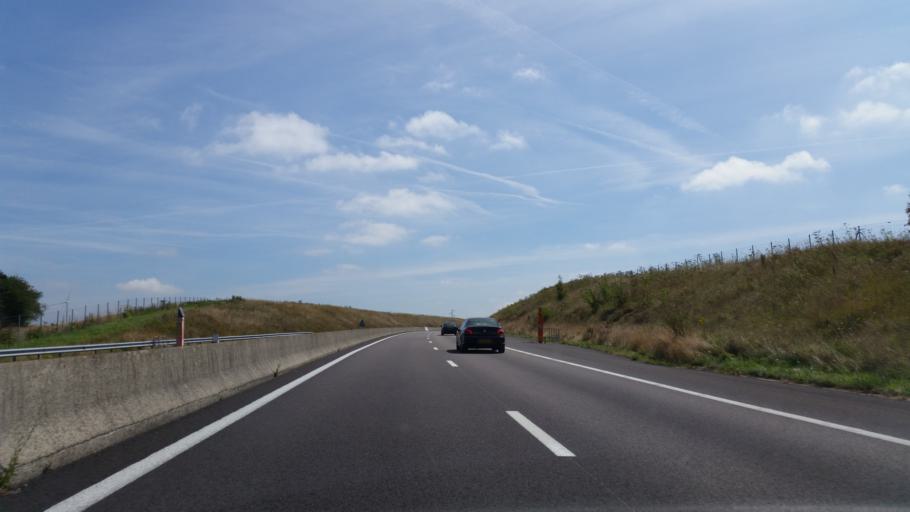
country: FR
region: Haute-Normandie
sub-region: Departement de la Seine-Maritime
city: Gaillefontaine
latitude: 49.7419
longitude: 1.5935
